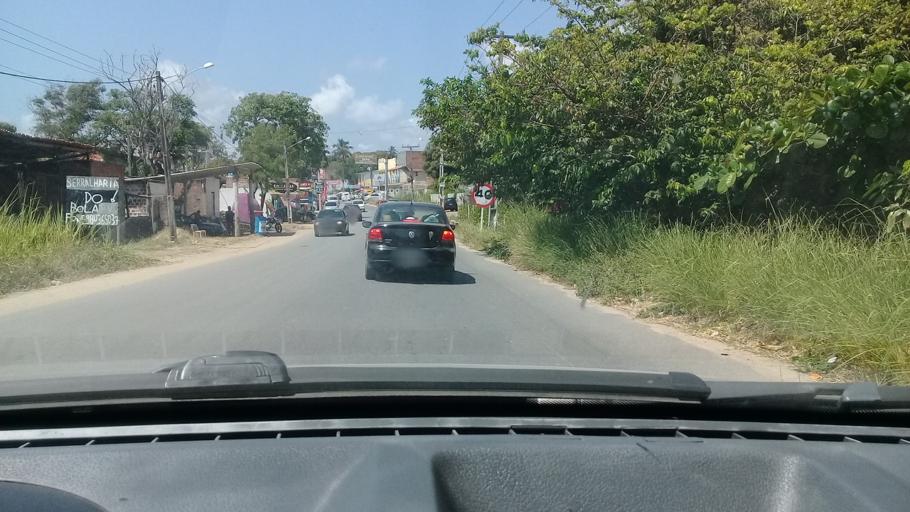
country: BR
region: Pernambuco
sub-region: Itamaraca
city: Itamaraca
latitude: -7.7850
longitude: -34.8391
